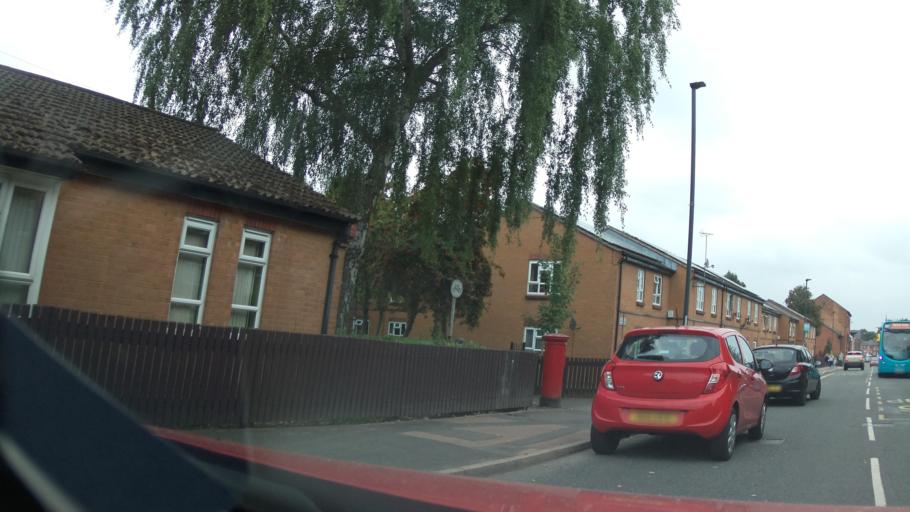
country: GB
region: England
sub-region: Derby
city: Derby
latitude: 52.9134
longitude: -1.4884
